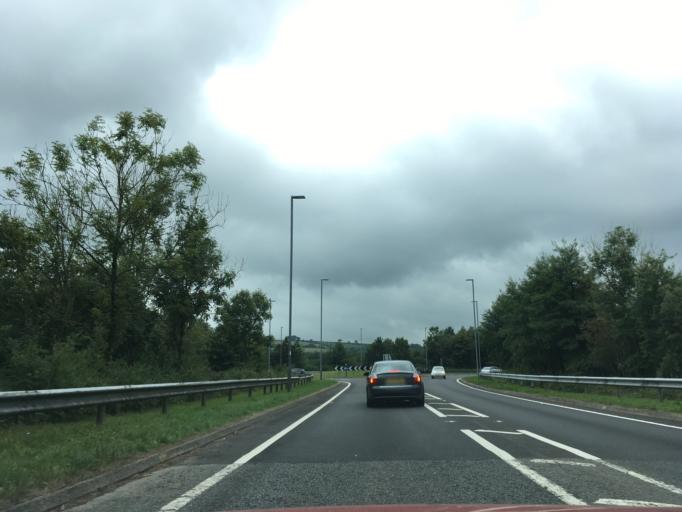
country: GB
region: Wales
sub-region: Carmarthenshire
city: Whitland
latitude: 51.8219
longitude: -4.6246
